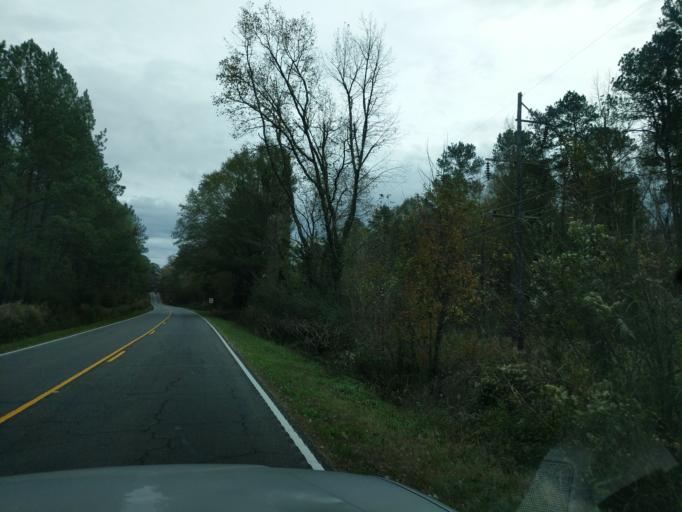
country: US
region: South Carolina
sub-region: Lexington County
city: Batesburg
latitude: 33.9478
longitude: -81.6274
